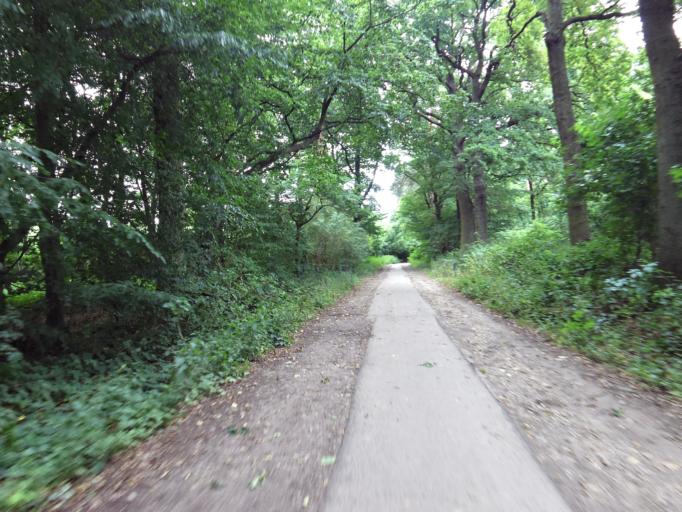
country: NL
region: Limburg
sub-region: Gemeente Heerlen
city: Heerlen
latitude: 50.9167
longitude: 6.0026
